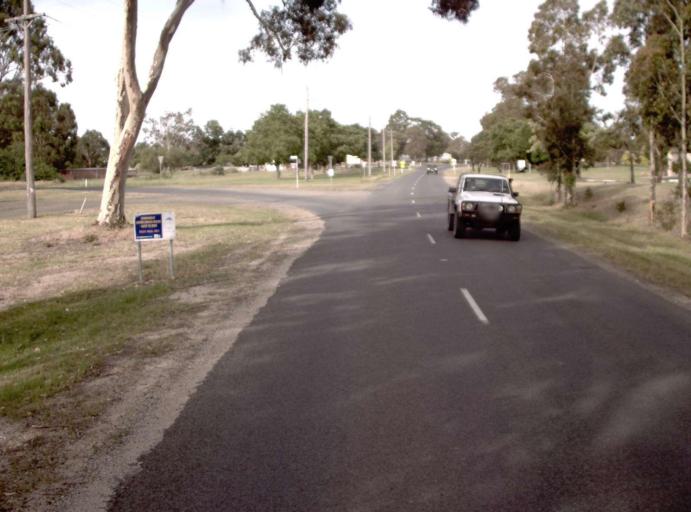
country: AU
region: Victoria
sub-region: Latrobe
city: Traralgon
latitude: -38.0619
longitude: 146.6218
